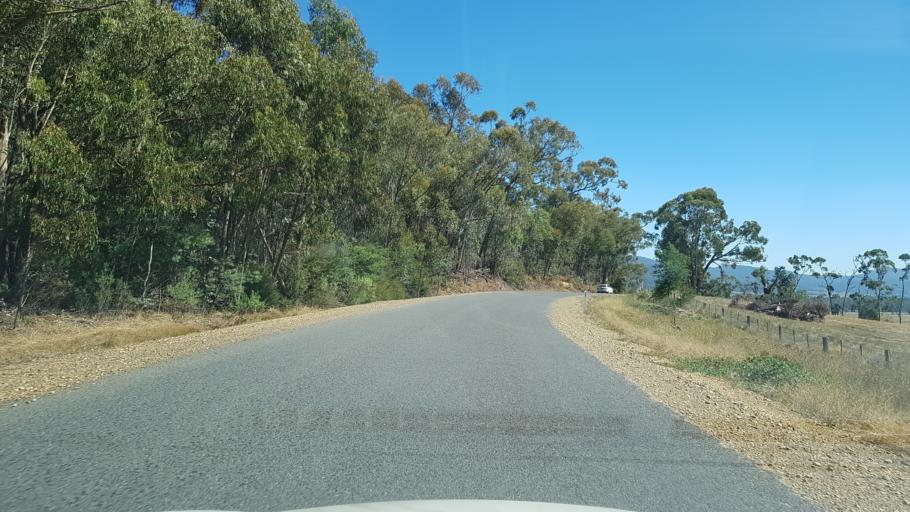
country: AU
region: Victoria
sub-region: Mansfield
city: Mansfield
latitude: -36.8146
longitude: 146.4500
